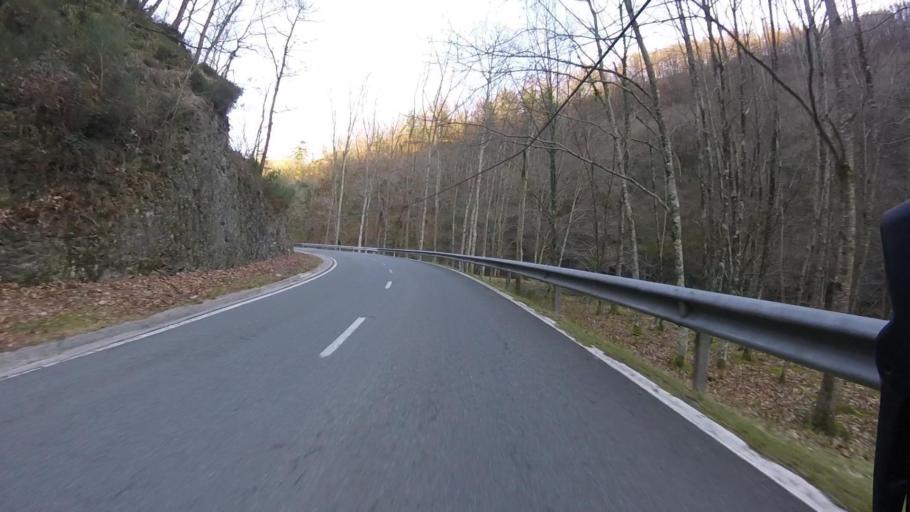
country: ES
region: Navarre
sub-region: Provincia de Navarra
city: Arano
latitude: 43.2078
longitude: -1.8675
